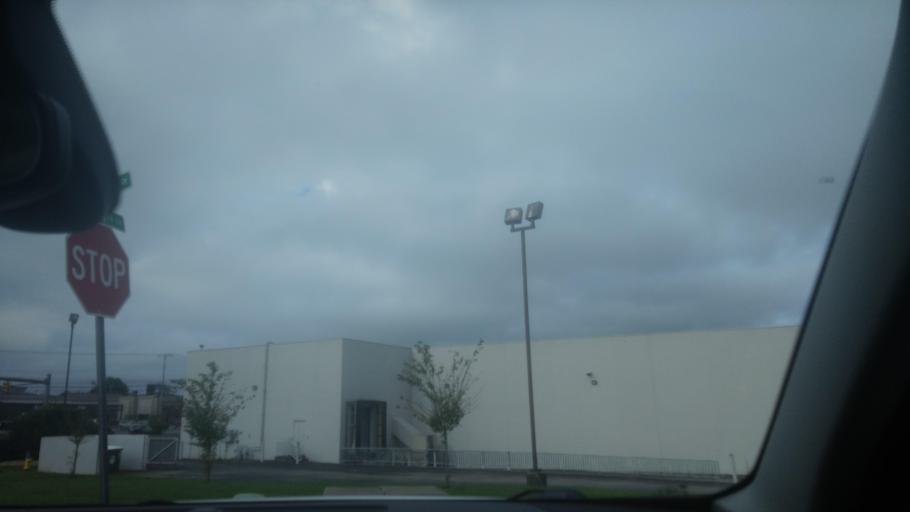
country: US
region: Tennessee
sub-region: Blount County
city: Alcoa
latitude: 35.7726
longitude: -83.9852
